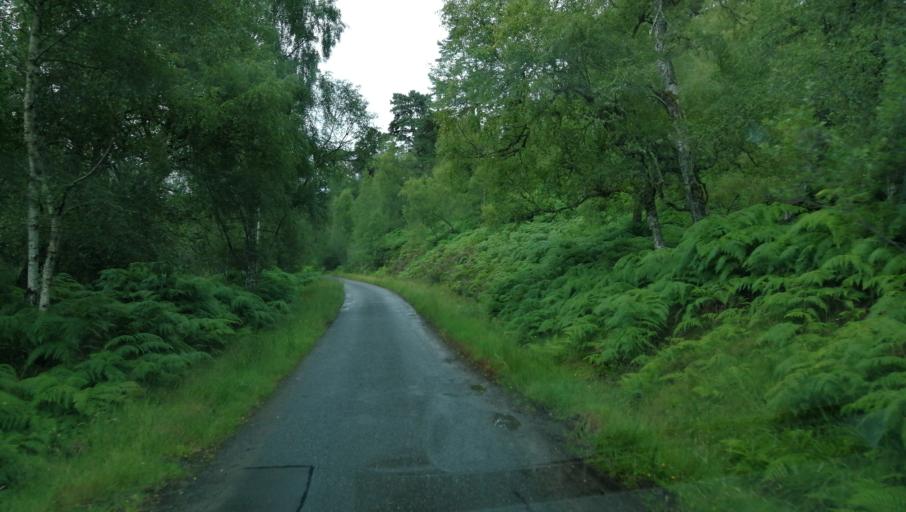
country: GB
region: Scotland
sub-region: Highland
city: Spean Bridge
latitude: 57.2905
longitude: -4.9181
